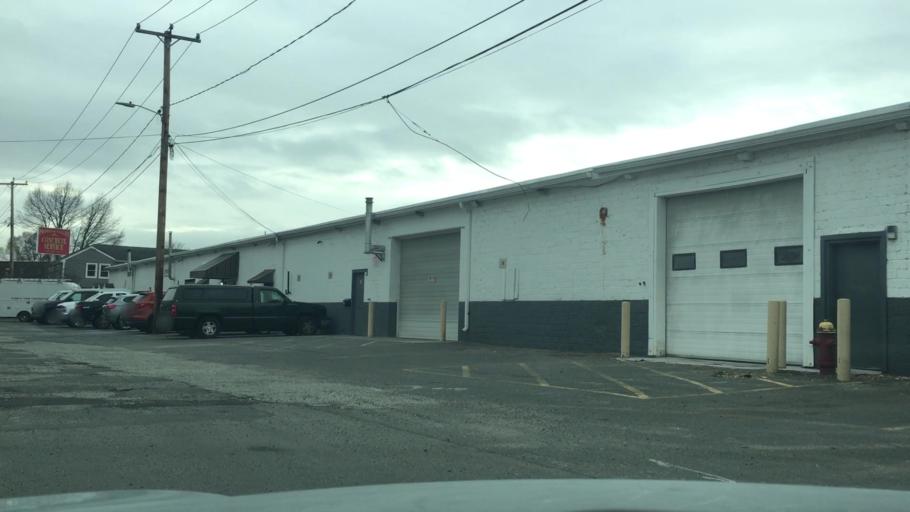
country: US
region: Massachusetts
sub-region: Hampden County
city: North Chicopee
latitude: 42.1944
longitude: -72.5987
